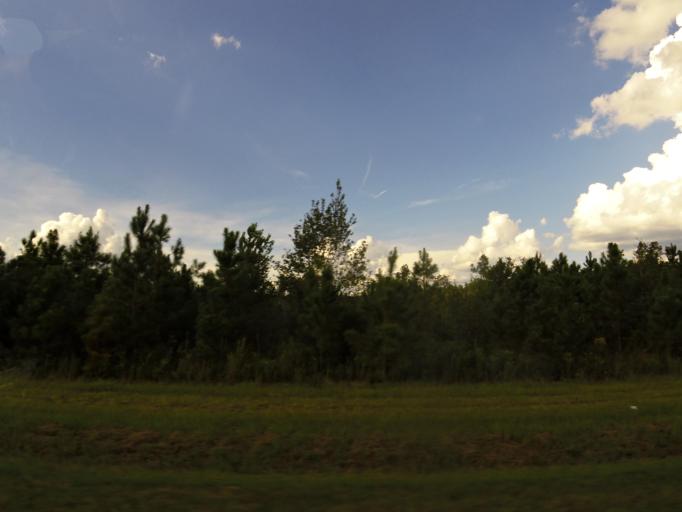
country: US
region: Georgia
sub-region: Brooks County
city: Quitman
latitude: 30.7918
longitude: -83.4753
